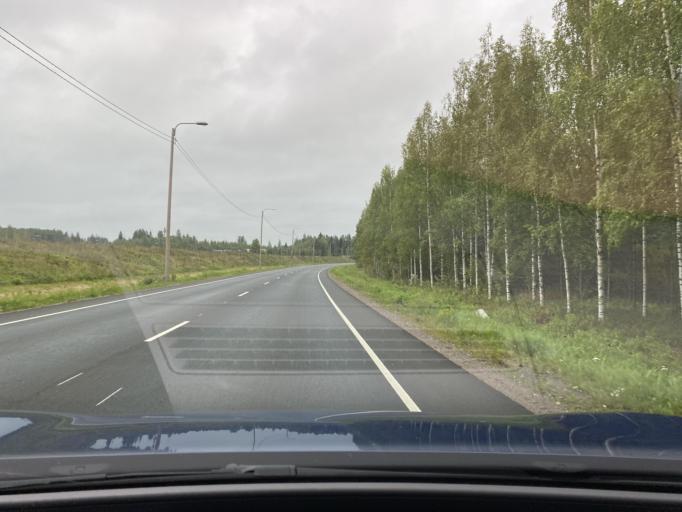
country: FI
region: Kymenlaakso
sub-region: Kouvola
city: Kouvola
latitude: 60.8890
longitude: 26.6046
